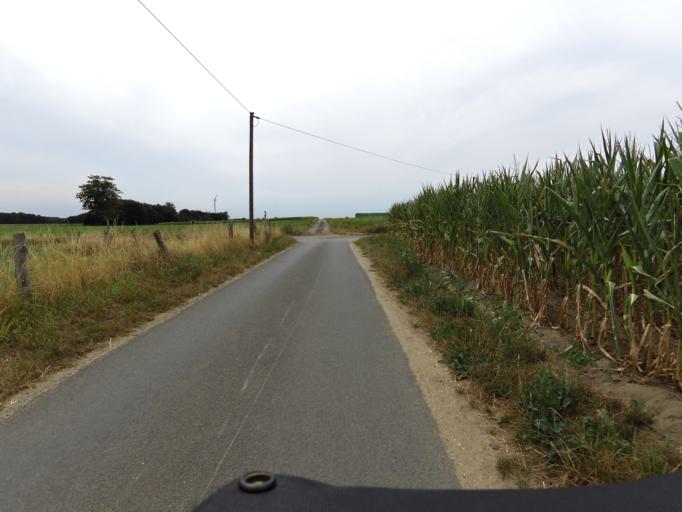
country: DE
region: North Rhine-Westphalia
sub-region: Regierungsbezirk Dusseldorf
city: Weeze
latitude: 51.5851
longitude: 6.1841
